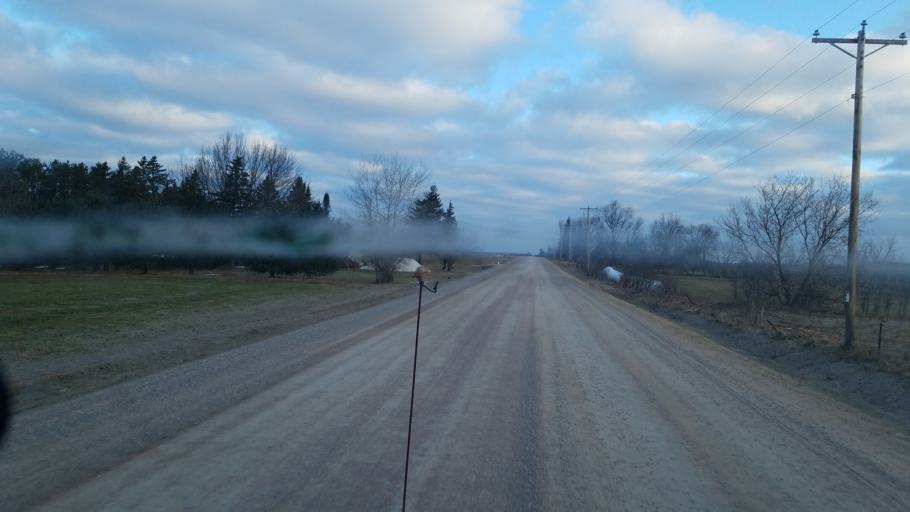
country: US
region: Wisconsin
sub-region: Clark County
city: Loyal
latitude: 44.6026
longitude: -90.4565
